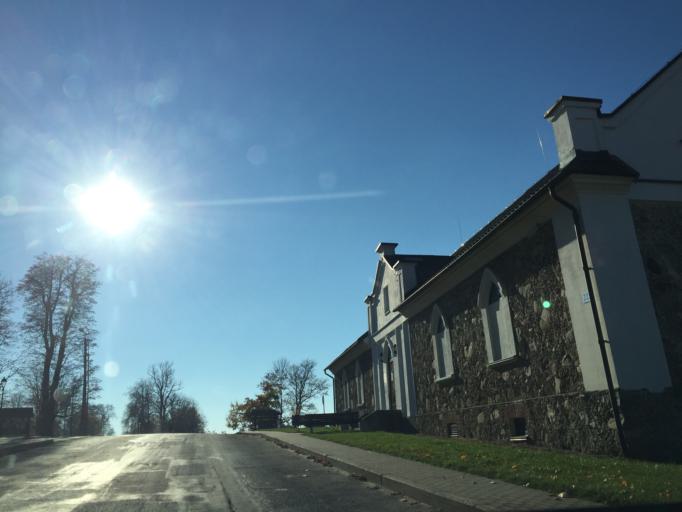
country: LT
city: Plateliai
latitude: 56.0385
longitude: 21.8149
